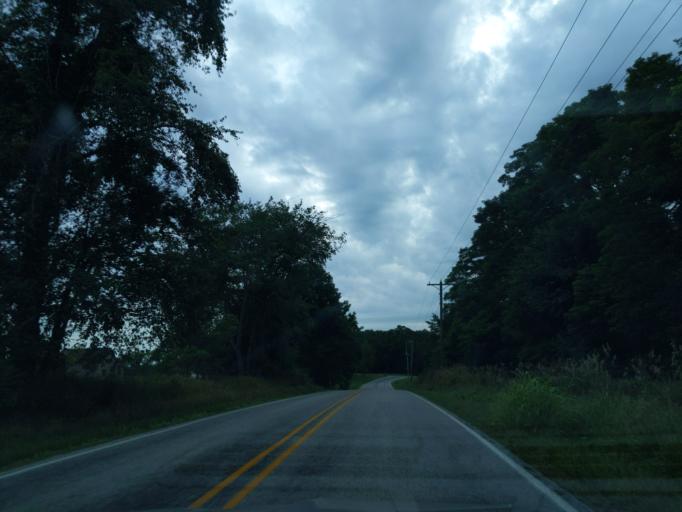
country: US
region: Indiana
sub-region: Ripley County
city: Osgood
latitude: 39.1924
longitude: -85.2178
